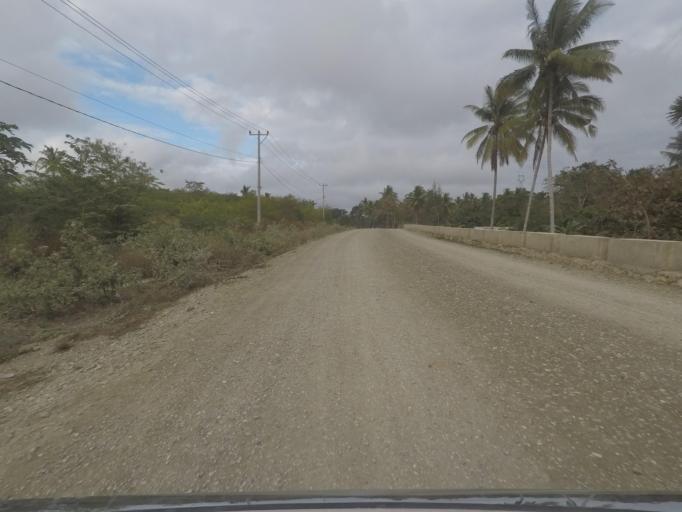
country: TL
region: Baucau
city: Baucau
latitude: -8.4986
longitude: 126.4517
